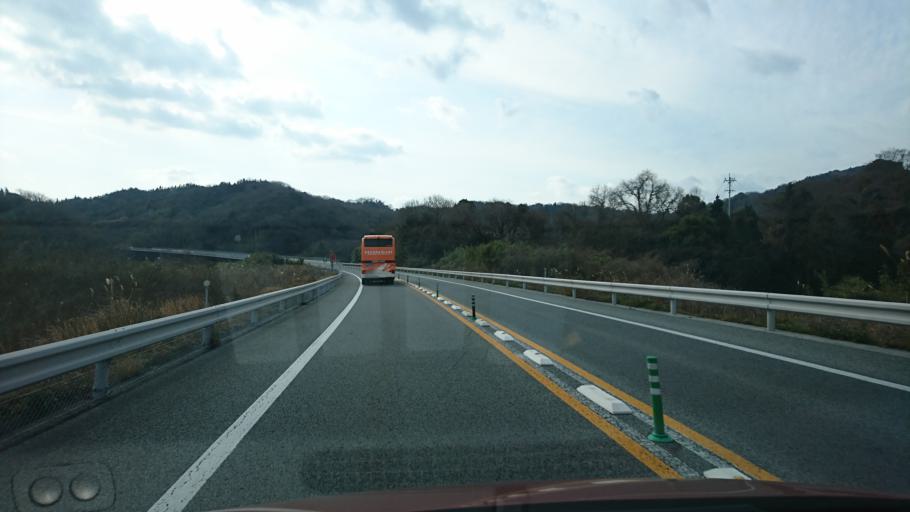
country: JP
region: Hiroshima
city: Innoshima
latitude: 34.1695
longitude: 133.0646
